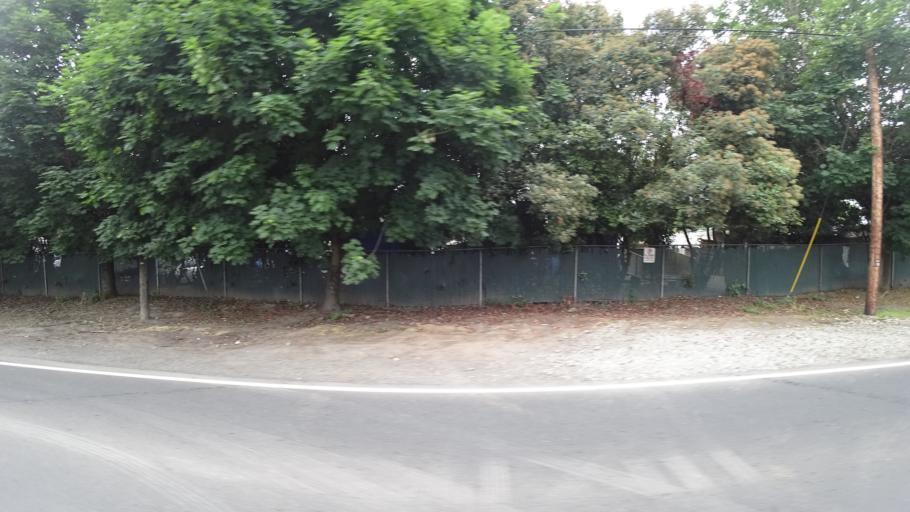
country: US
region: Washington
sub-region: Clark County
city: Vancouver
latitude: 45.5902
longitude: -122.6629
